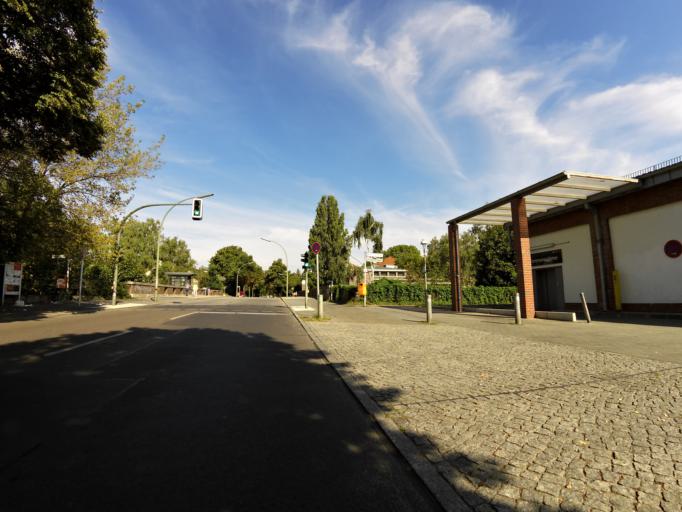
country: DE
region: Berlin
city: Zehlendorf Bezirk
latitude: 52.4357
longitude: 13.2739
